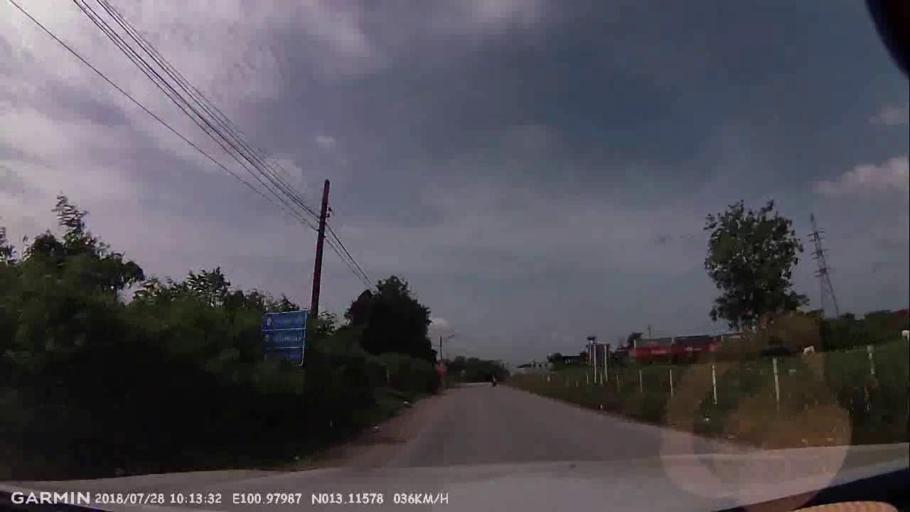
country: TH
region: Chon Buri
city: Ban Talat Bueng
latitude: 13.1157
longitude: 100.9799
